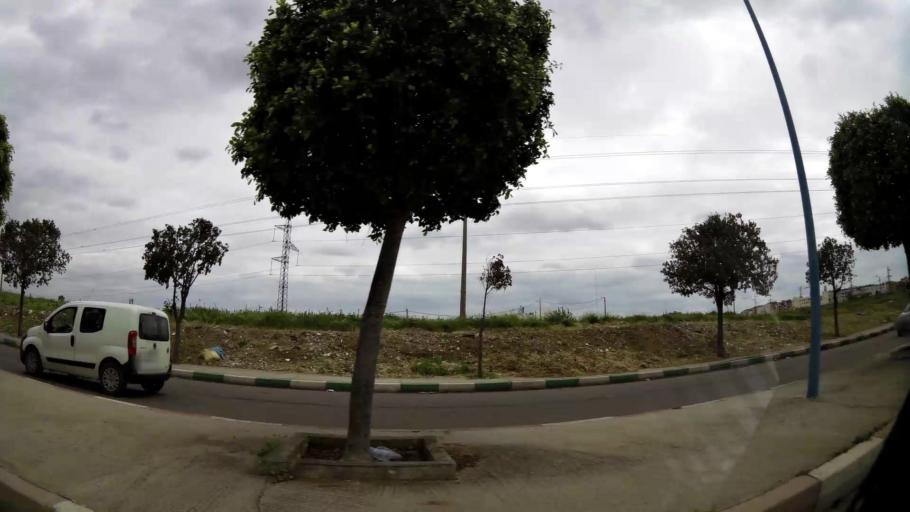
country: MA
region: Grand Casablanca
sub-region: Casablanca
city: Casablanca
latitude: 33.5931
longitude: -7.5518
